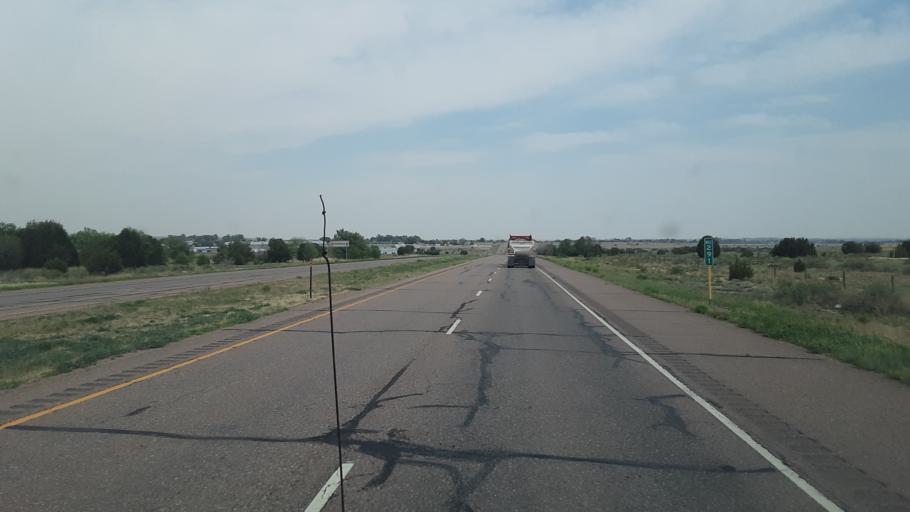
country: US
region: Colorado
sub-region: Fremont County
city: Penrose
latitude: 38.4130
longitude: -105.0208
